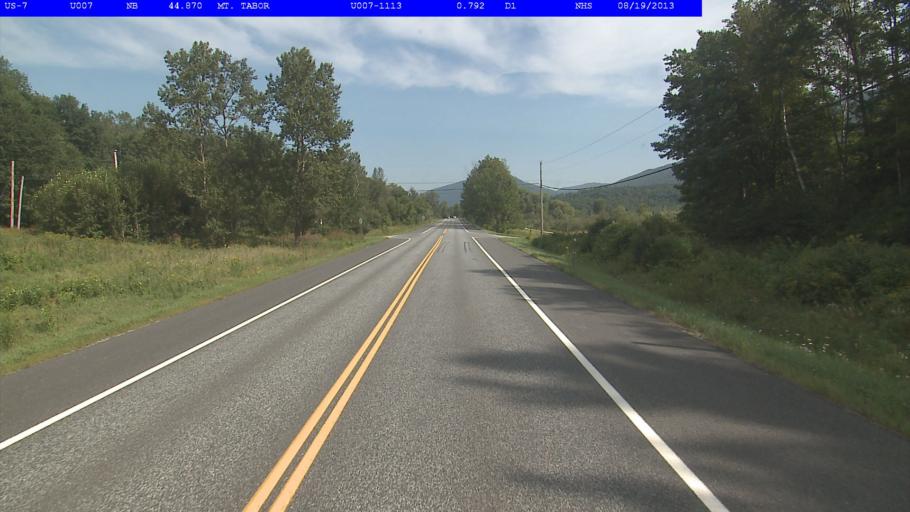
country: US
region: Vermont
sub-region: Bennington County
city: Manchester Center
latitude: 43.3163
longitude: -72.9920
